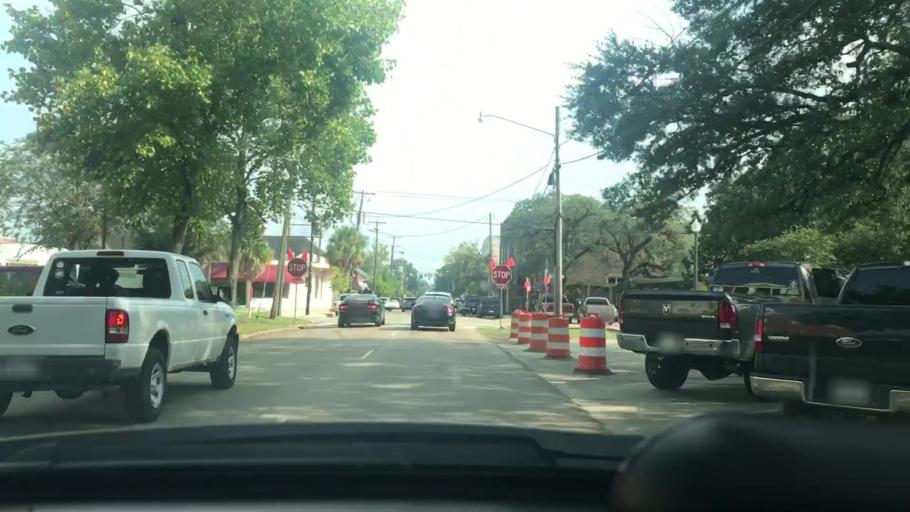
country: US
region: Louisiana
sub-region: Tangipahoa Parish
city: Hammond
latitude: 30.5053
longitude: -90.4628
